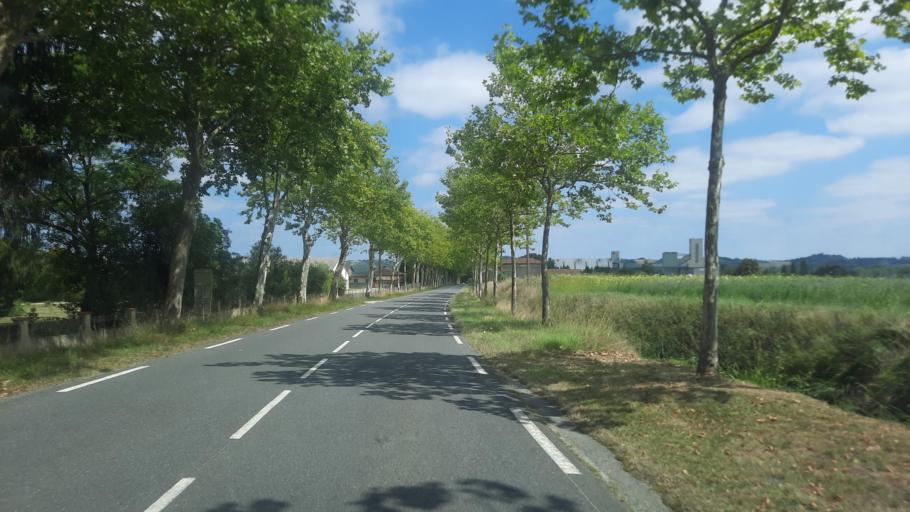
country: FR
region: Midi-Pyrenees
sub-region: Departement de la Haute-Garonne
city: Boulogne-sur-Gesse
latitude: 43.2927
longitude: 0.6529
